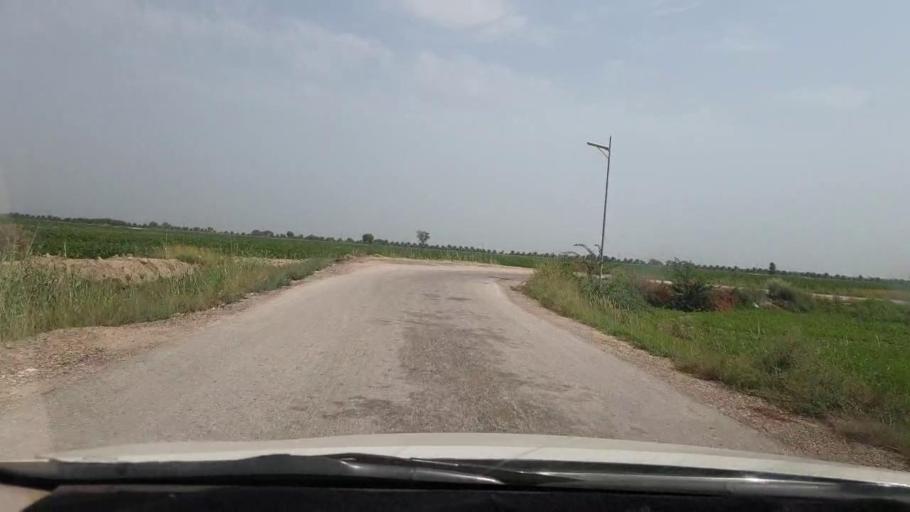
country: PK
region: Sindh
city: Rohri
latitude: 27.5382
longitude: 69.0043
